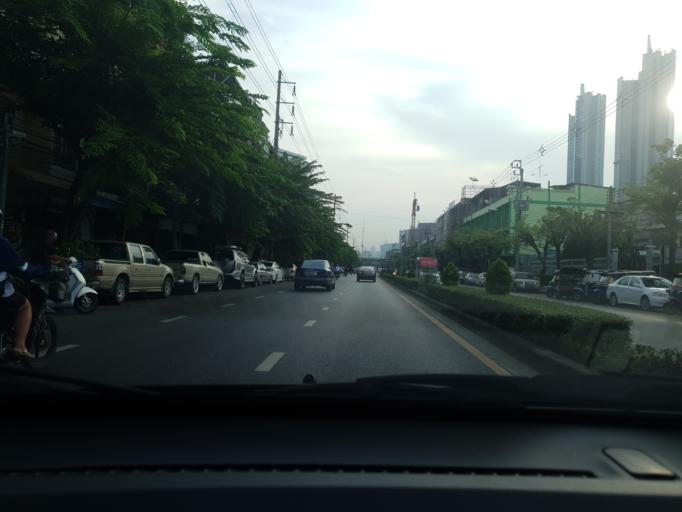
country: TH
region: Bangkok
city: Khlong San
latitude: 13.7288
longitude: 100.5034
